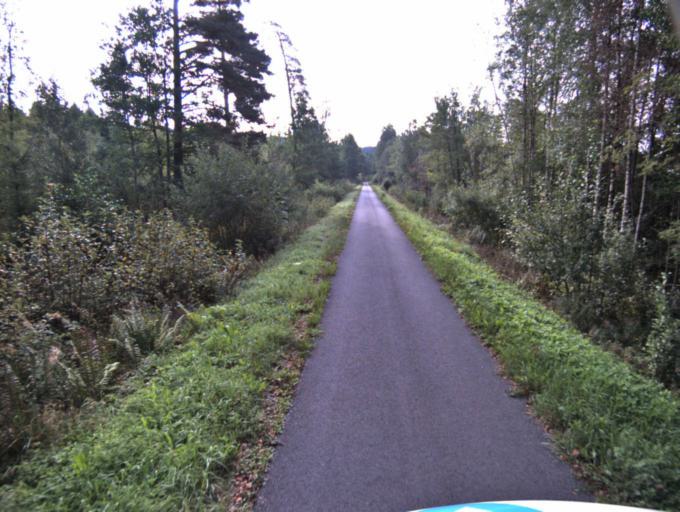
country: SE
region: Vaestra Goetaland
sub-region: Ulricehamns Kommun
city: Ulricehamn
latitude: 57.7117
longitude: 13.3955
